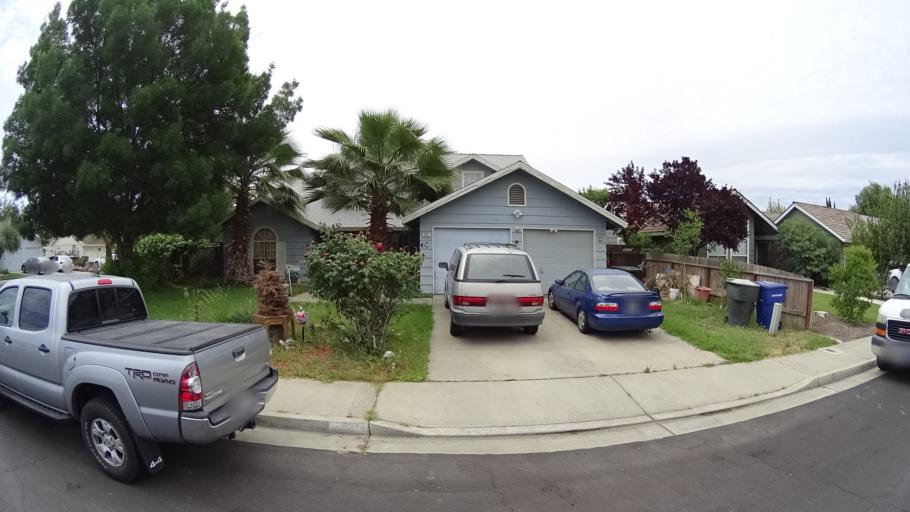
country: US
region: California
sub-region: Kings County
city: Lucerne
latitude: 36.3605
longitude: -119.6400
